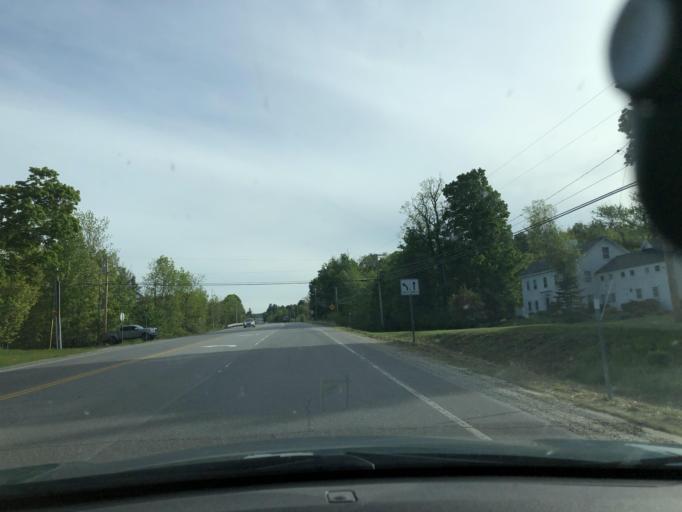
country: US
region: New Hampshire
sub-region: Merrimack County
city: New London
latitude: 43.4104
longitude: -71.9515
